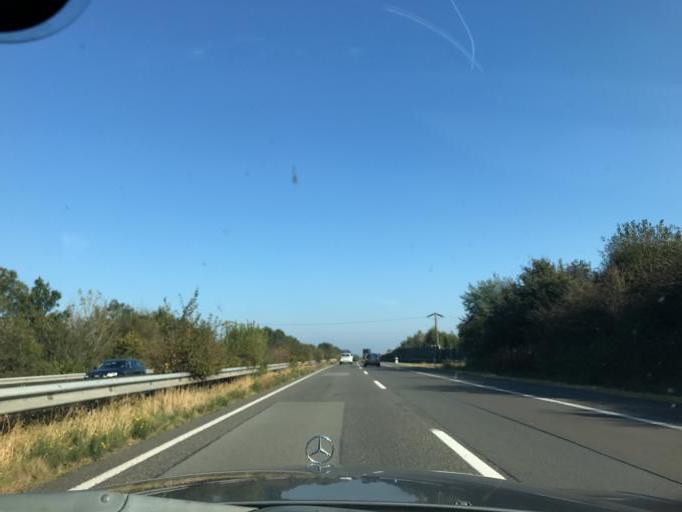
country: DE
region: Lower Saxony
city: Leer
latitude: 53.2643
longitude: 7.4615
